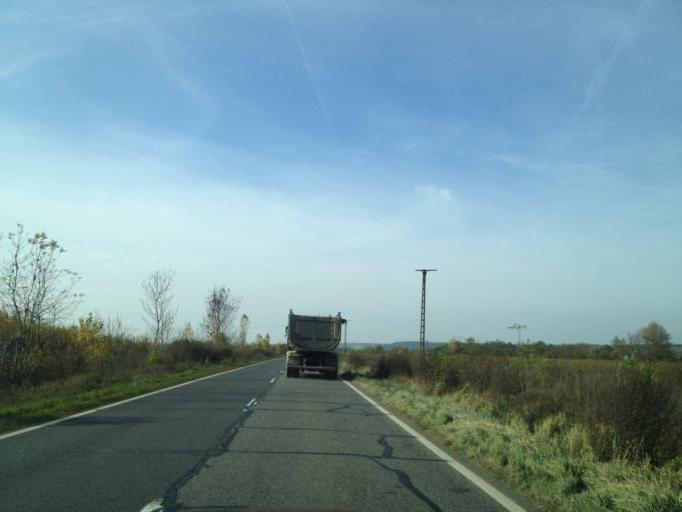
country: RO
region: Timis
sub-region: Comuna Faget
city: Faget
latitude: 45.8581
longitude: 22.2212
